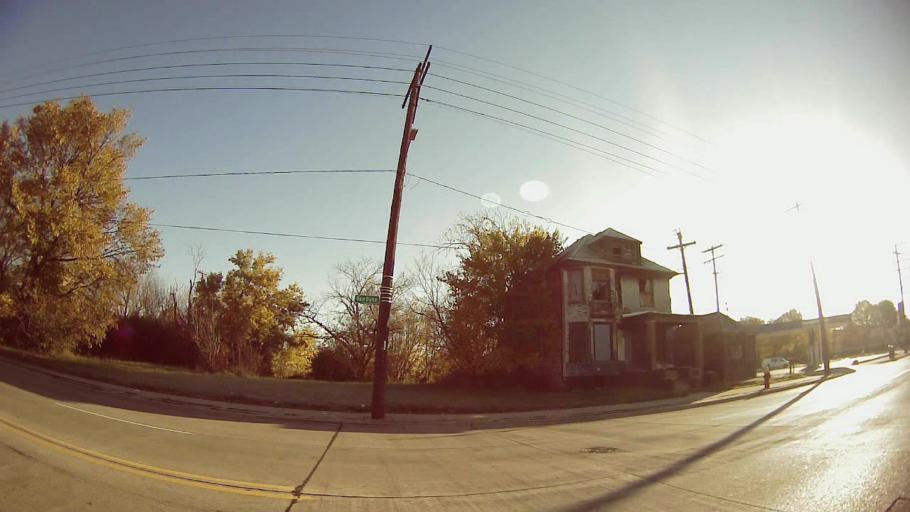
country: US
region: Michigan
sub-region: Wayne County
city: Hamtramck
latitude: 42.3798
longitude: -83.0155
